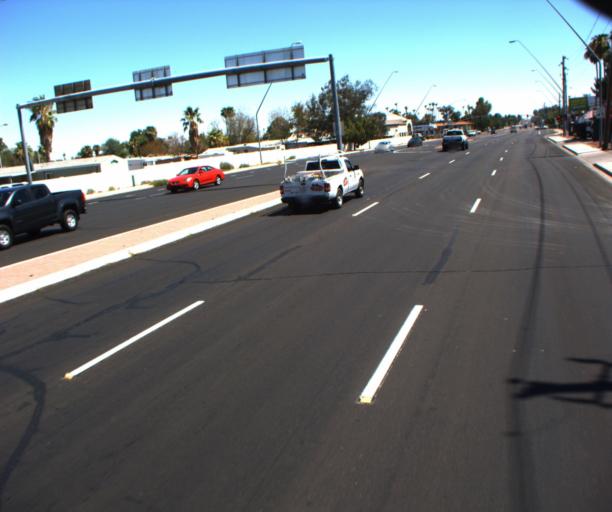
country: US
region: Arizona
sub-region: Maricopa County
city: Mesa
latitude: 33.4537
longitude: -111.8399
